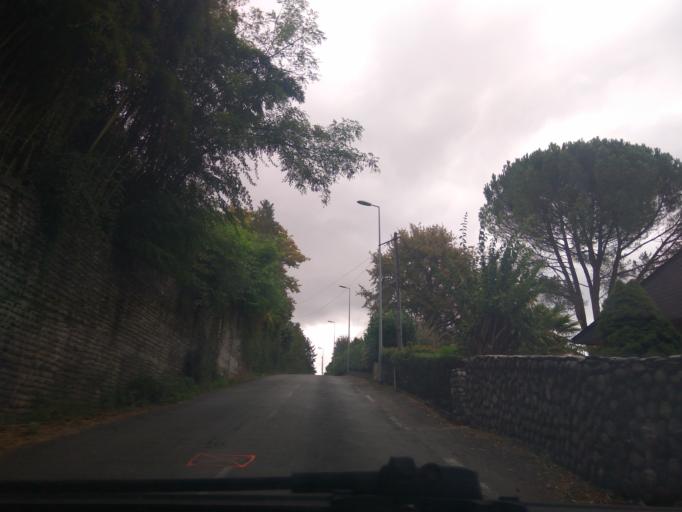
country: FR
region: Aquitaine
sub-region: Departement des Pyrenees-Atlantiques
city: Bizanos
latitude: 43.2967
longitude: -0.3356
